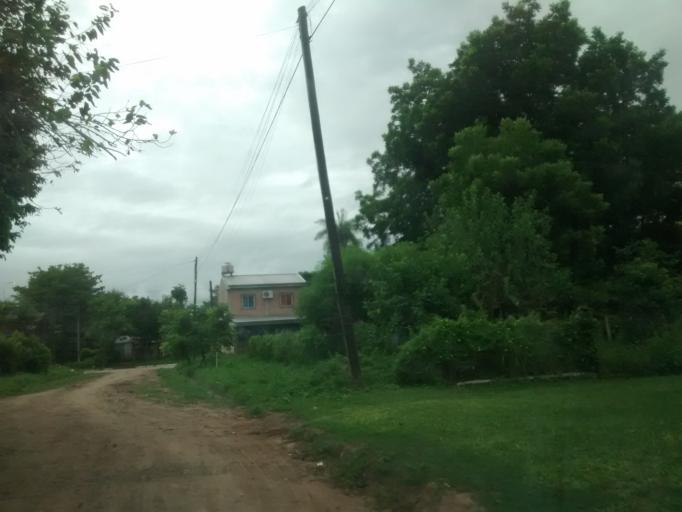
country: AR
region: Chaco
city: Puerto Tirol
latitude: -27.3708
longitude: -59.0935
